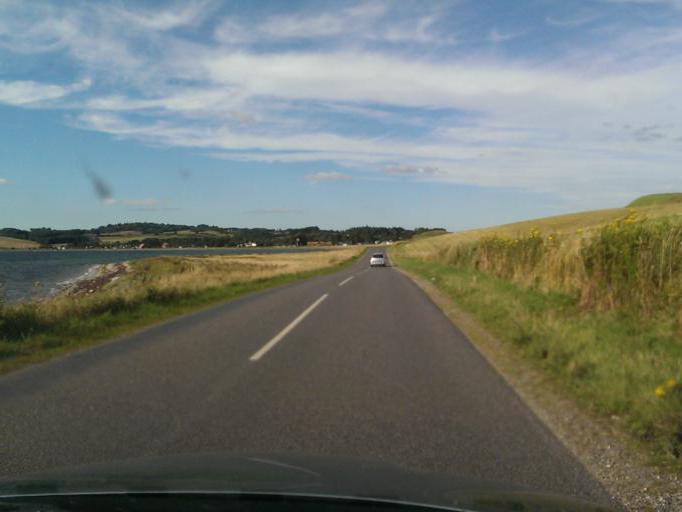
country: DK
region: Central Jutland
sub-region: Syddjurs Kommune
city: Ronde
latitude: 56.1610
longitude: 10.5274
